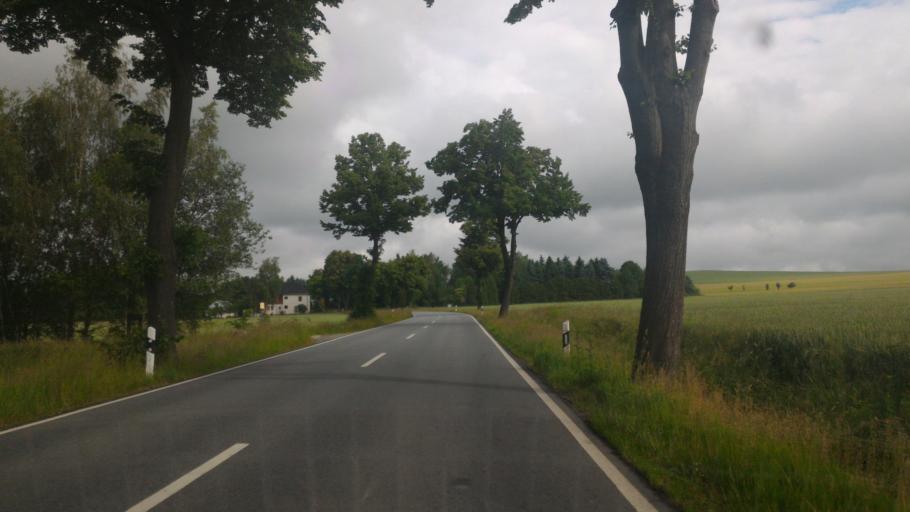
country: DE
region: Saxony
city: Neugersdorf
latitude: 50.9765
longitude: 14.6357
